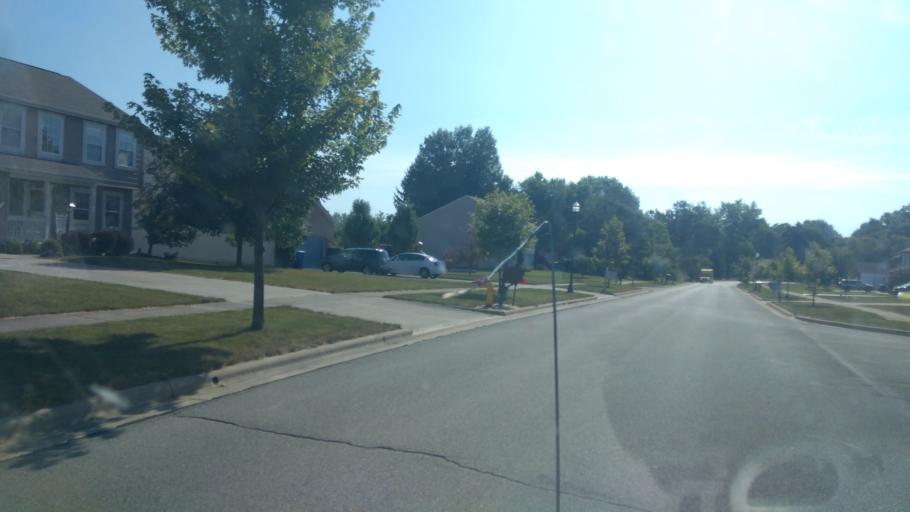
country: US
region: Ohio
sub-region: Delaware County
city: Delaware
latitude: 40.3243
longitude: -83.0757
